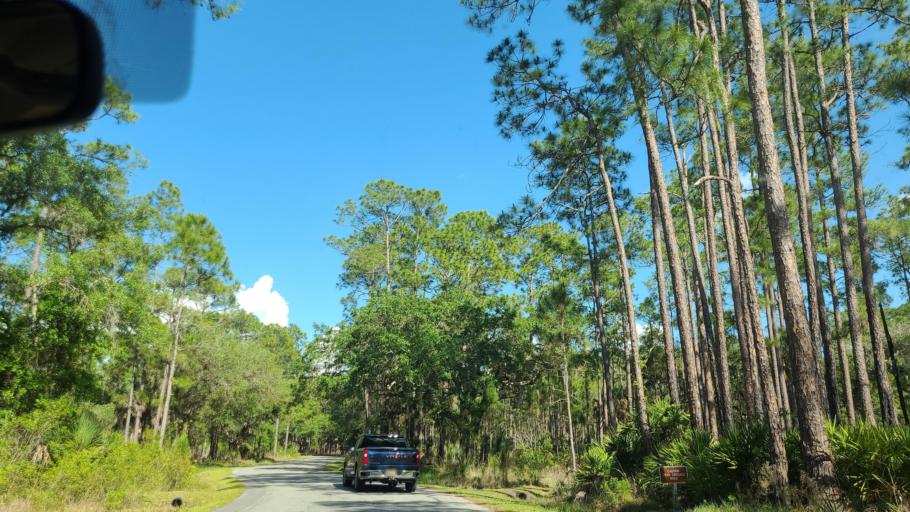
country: US
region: Florida
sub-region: Polk County
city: Babson Park
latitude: 27.9525
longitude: -81.3728
